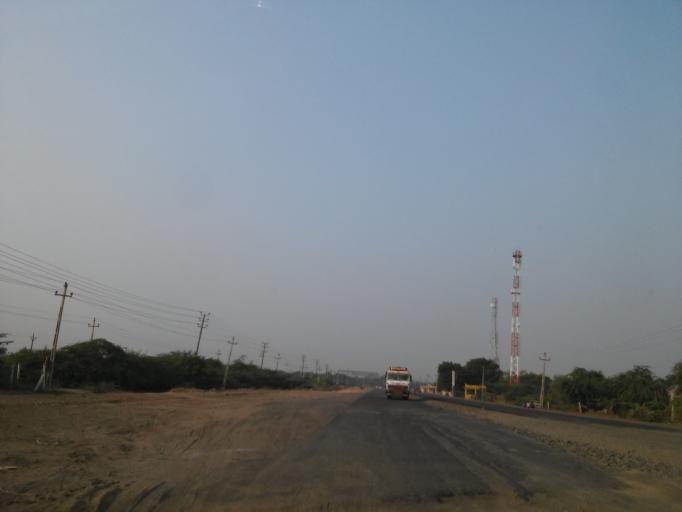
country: IN
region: Gujarat
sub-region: Kachchh
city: Bhachau
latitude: 23.3330
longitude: 70.2266
